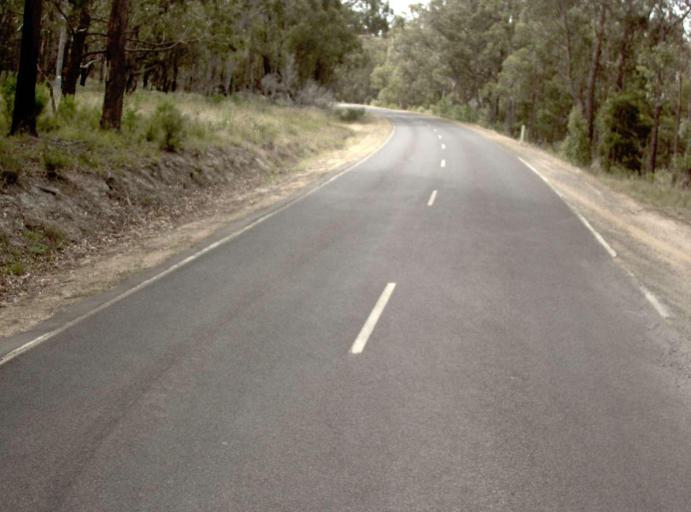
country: AU
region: Victoria
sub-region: Latrobe
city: Traralgon
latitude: -38.4033
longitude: 146.8238
